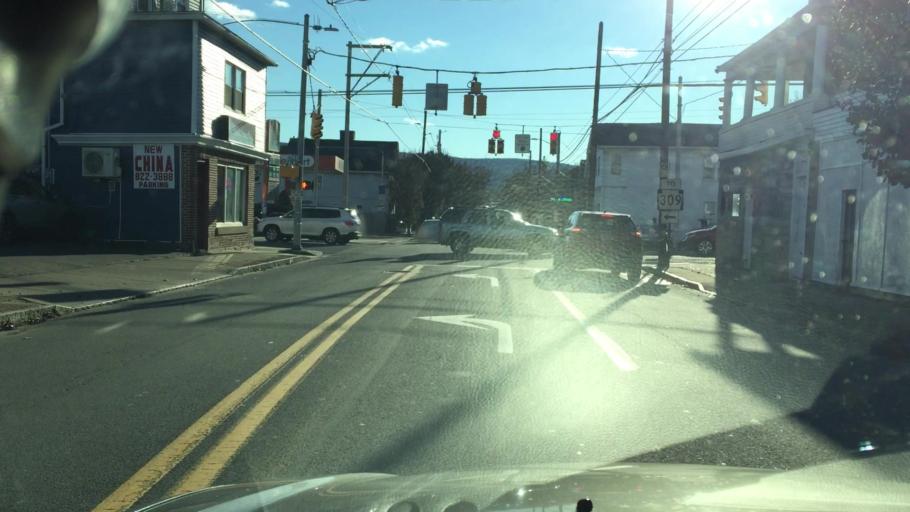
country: US
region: Pennsylvania
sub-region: Luzerne County
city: Ashley
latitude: 41.2272
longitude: -75.8932
